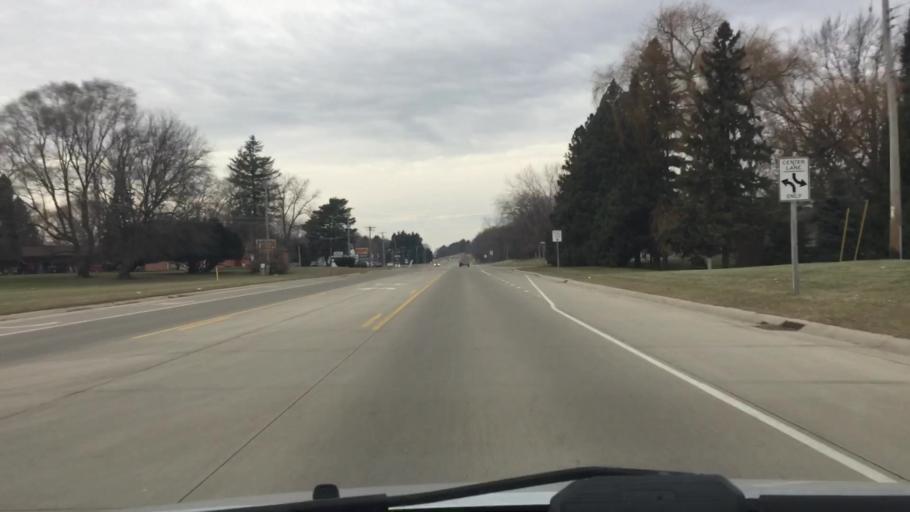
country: US
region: Wisconsin
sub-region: Waukesha County
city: Oconomowoc
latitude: 43.1262
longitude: -88.5333
